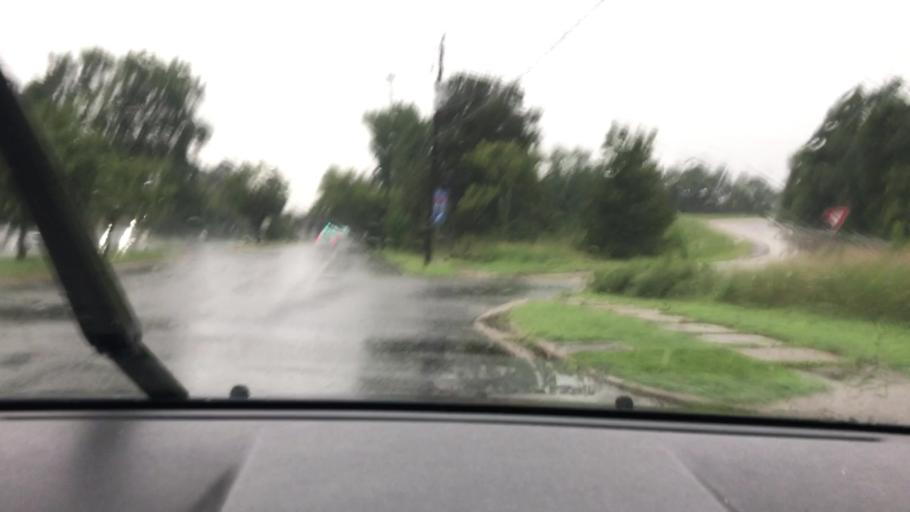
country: US
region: Virginia
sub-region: Henrico County
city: Lakeside
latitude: 37.5841
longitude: -77.4671
